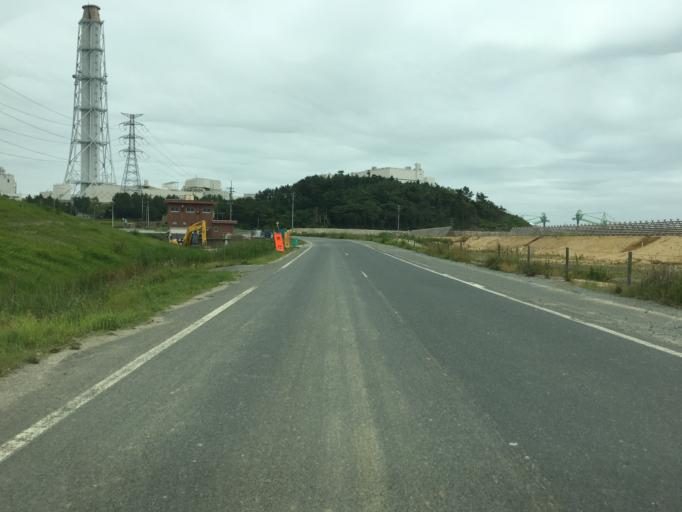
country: JP
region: Fukushima
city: Namie
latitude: 37.6602
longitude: 141.0152
